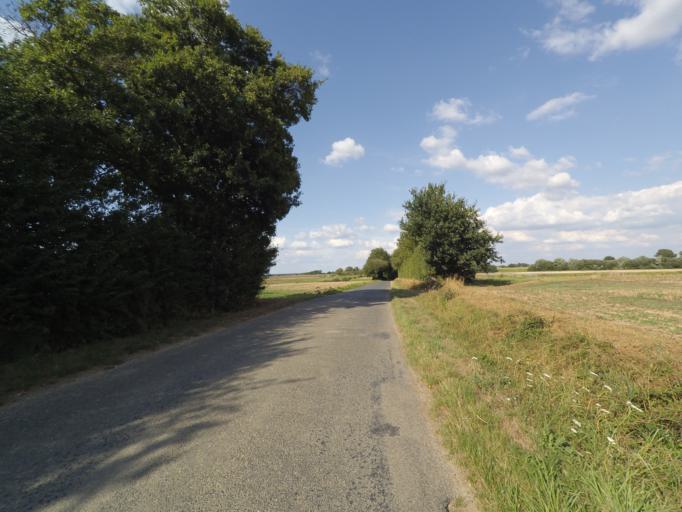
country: FR
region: Pays de la Loire
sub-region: Departement de la Loire-Atlantique
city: Vieillevigne
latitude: 46.9880
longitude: -1.4228
